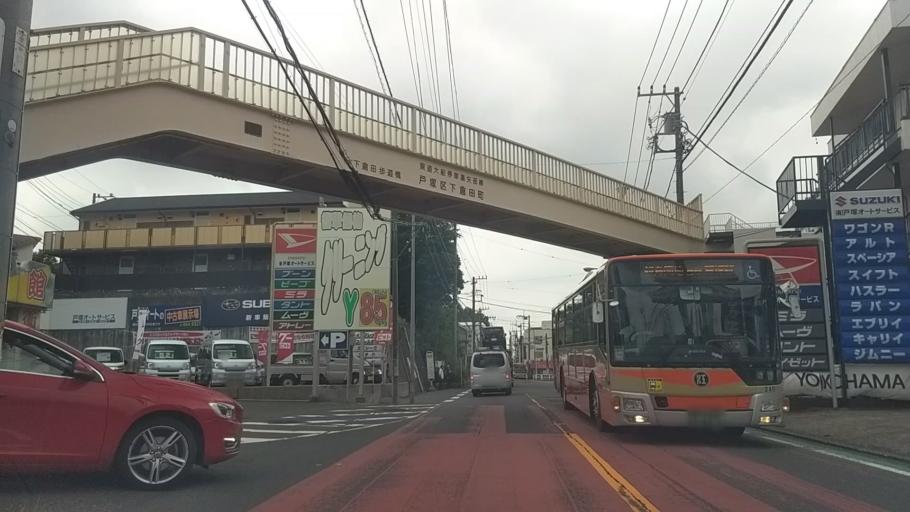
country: JP
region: Kanagawa
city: Kamakura
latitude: 35.3843
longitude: 139.5362
